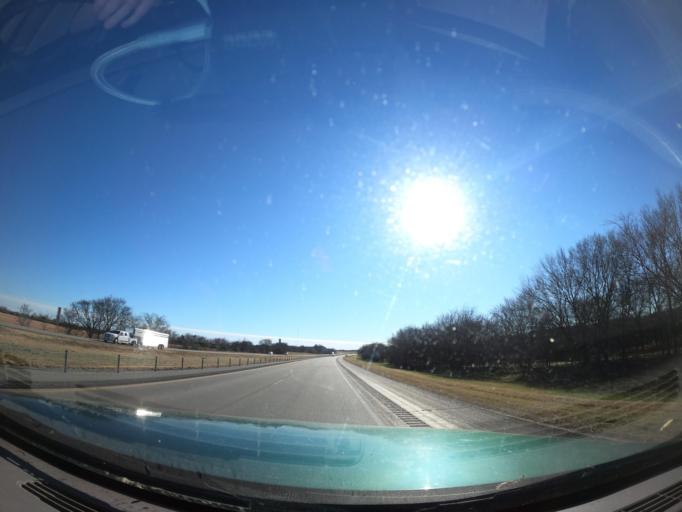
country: US
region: Oklahoma
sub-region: McIntosh County
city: Checotah
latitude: 35.4149
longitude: -95.5568
